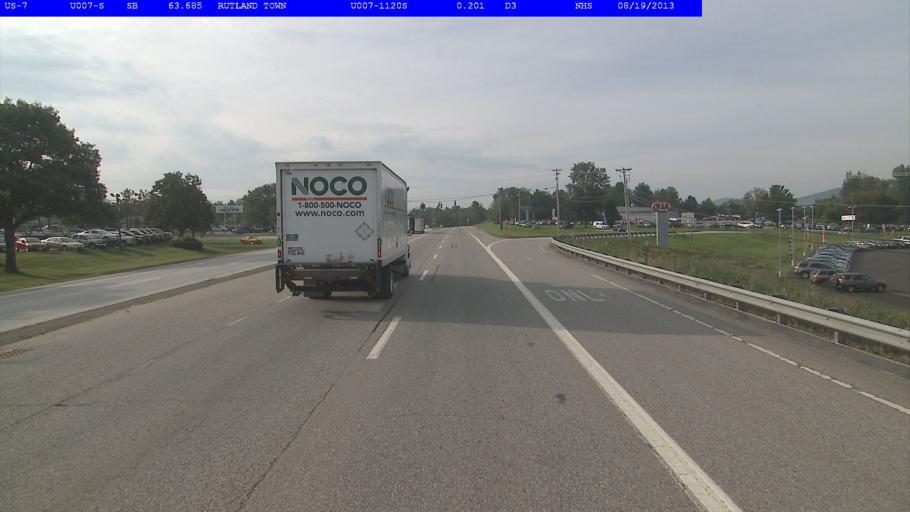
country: US
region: Vermont
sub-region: Rutland County
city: Rutland
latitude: 43.5761
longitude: -72.9664
